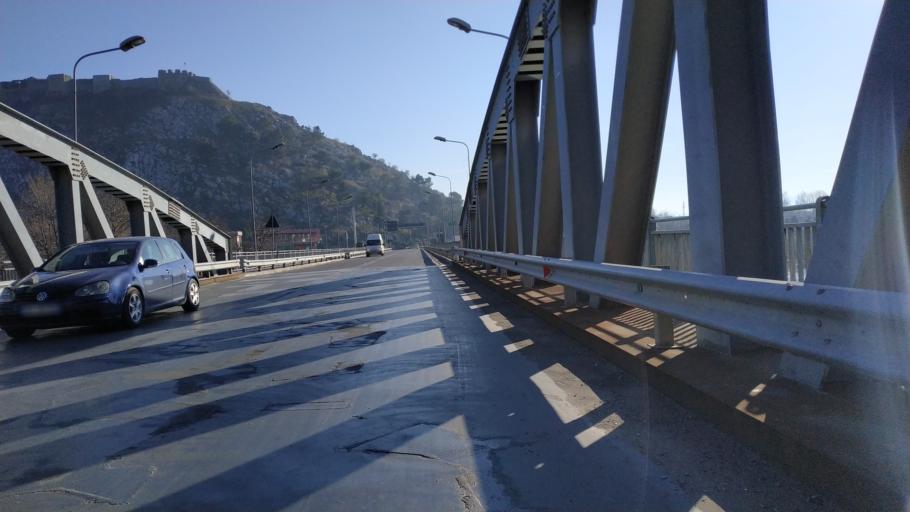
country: AL
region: Shkoder
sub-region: Rrethi i Shkodres
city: Berdica e Madhe
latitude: 42.0458
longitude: 19.4869
